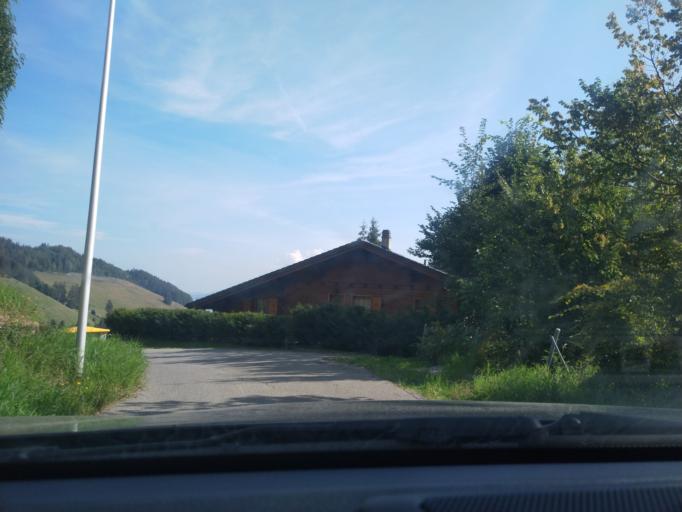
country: CH
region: Fribourg
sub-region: Gruyere District
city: Gruyeres
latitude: 46.5689
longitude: 7.0391
